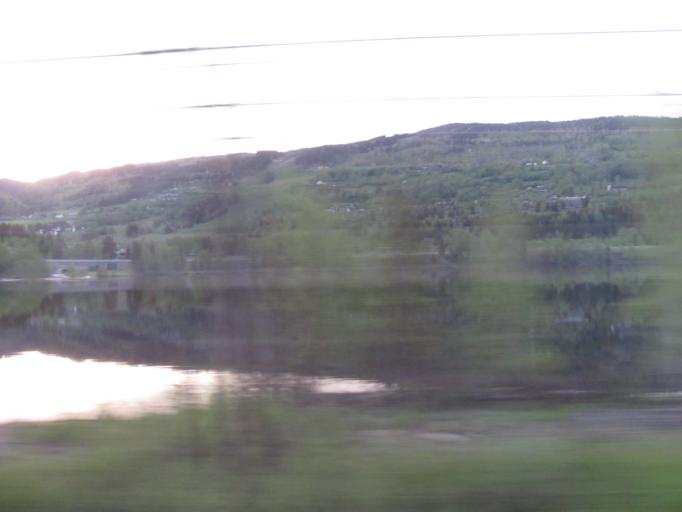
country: NO
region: Oppland
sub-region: Lillehammer
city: Lillehammer
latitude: 61.2293
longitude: 10.4378
